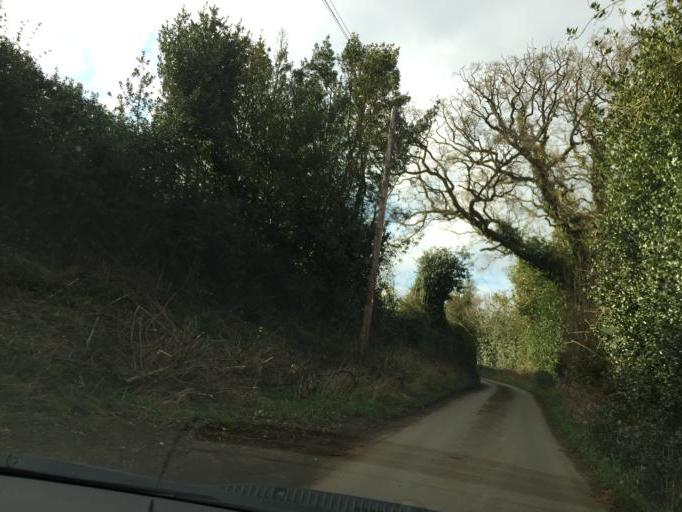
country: GB
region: England
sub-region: Solihull
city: Meriden
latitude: 52.4467
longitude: -1.5938
